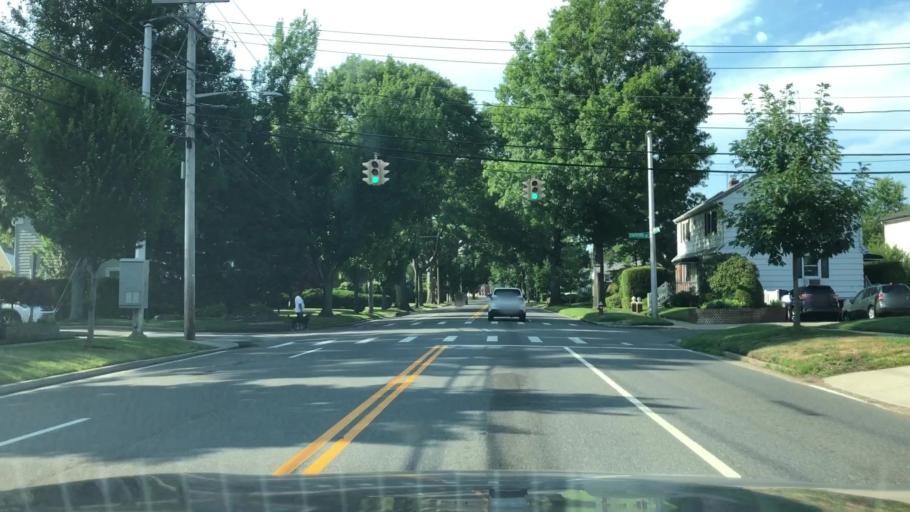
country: US
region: New York
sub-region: Nassau County
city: New Hyde Park
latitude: 40.7270
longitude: -73.6791
